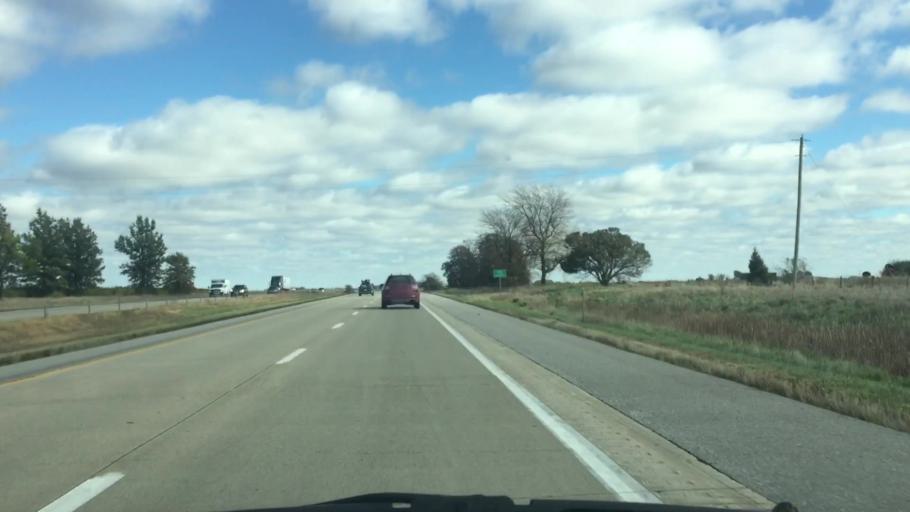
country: US
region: Iowa
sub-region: Poweshiek County
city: Brooklyn
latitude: 41.6956
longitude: -92.3006
